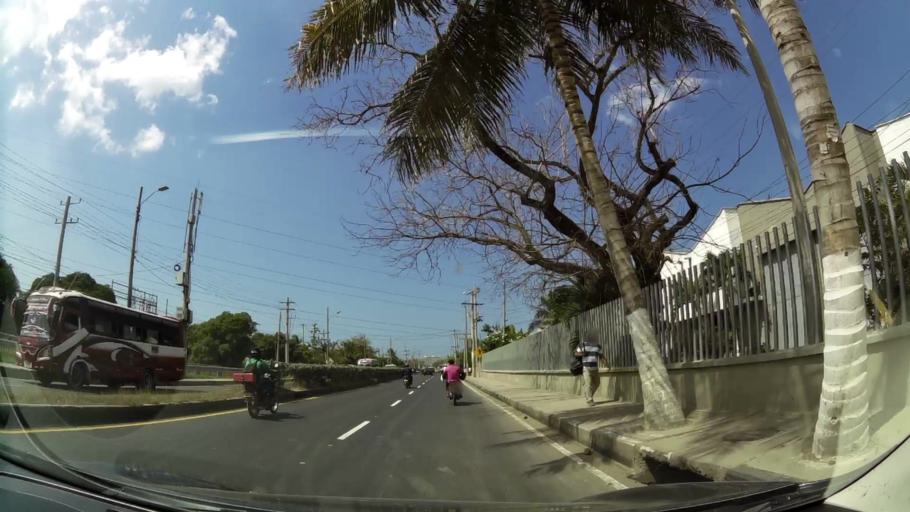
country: CO
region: Bolivar
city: Cartagena
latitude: 10.3780
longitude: -75.4617
